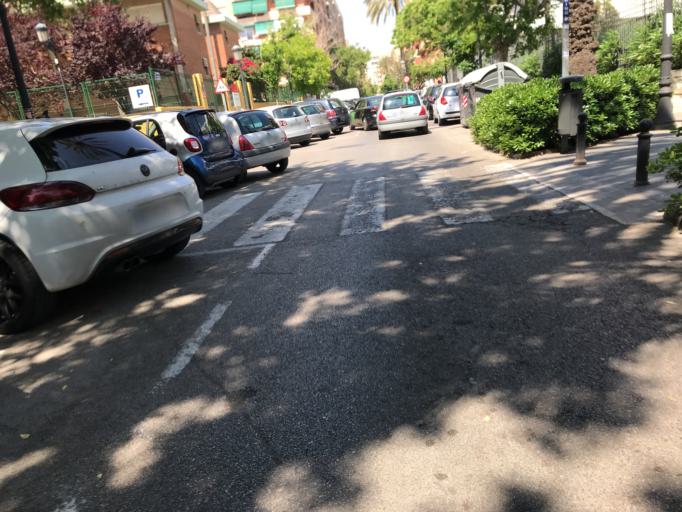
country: ES
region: Valencia
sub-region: Provincia de Valencia
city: Valencia
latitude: 39.4693
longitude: -0.3506
